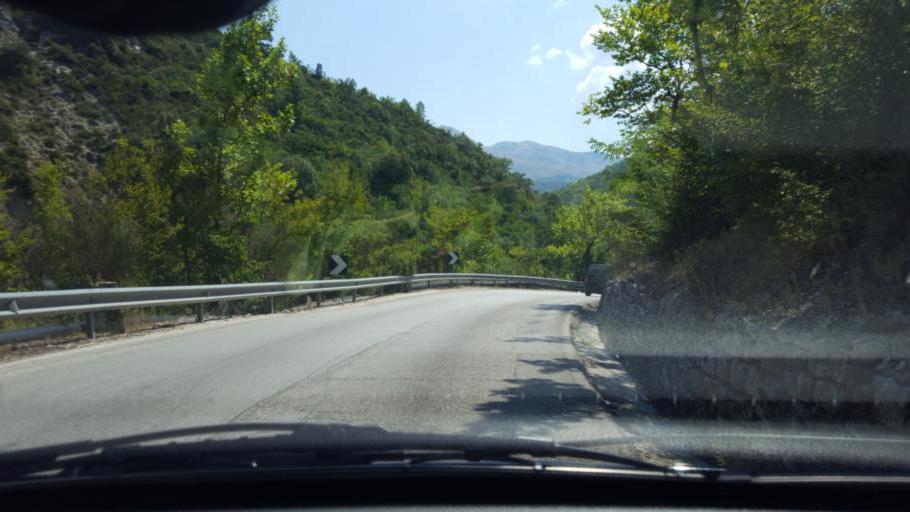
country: AL
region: Vlore
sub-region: Rrethi i Delvines
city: Delvine
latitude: 39.9226
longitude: 20.1638
